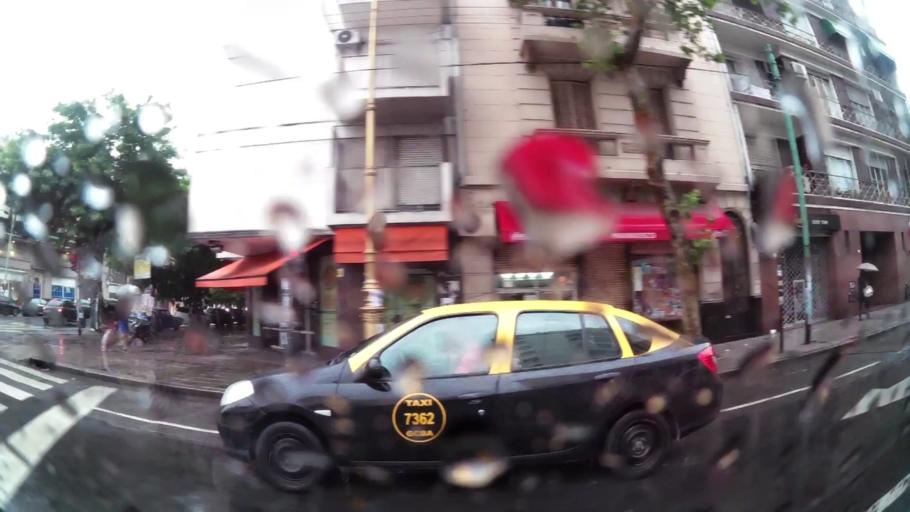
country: AR
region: Buenos Aires
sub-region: Partido de Avellaneda
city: Avellaneda
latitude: -34.6389
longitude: -58.3746
